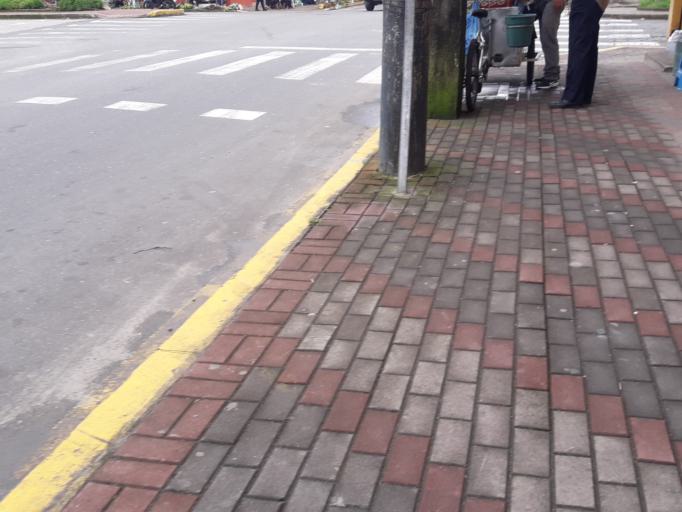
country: EC
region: Napo
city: Tena
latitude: -0.9995
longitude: -77.8133
